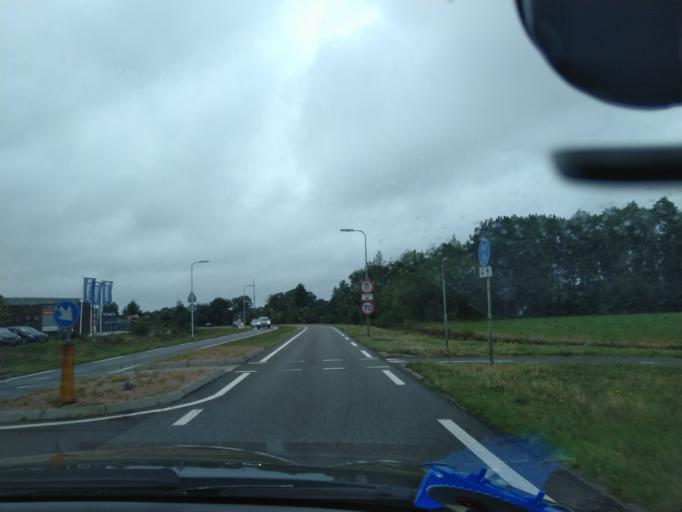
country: DE
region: Lower Saxony
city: Nordhorn
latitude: 52.3820
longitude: 7.0250
